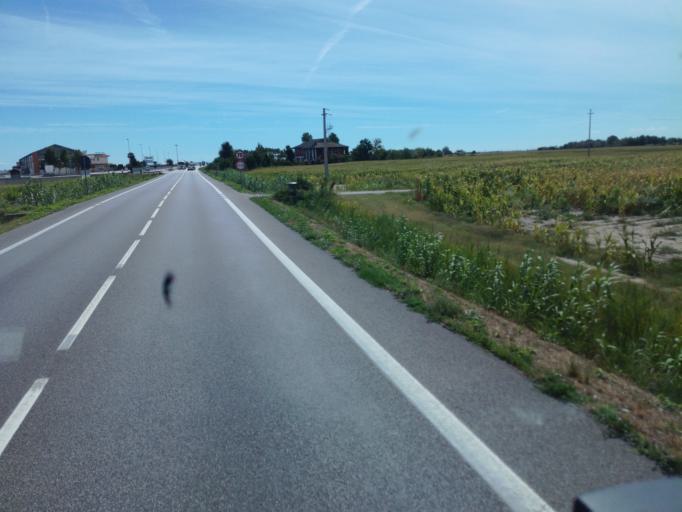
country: IT
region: Veneto
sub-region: Provincia di Venezia
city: Valli
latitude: 45.2221
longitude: 12.2054
